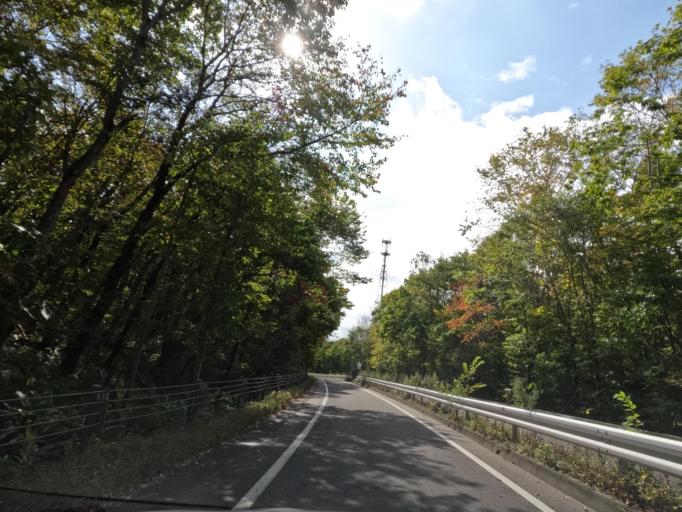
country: JP
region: Hokkaido
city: Chitose
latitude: 42.8018
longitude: 141.5694
